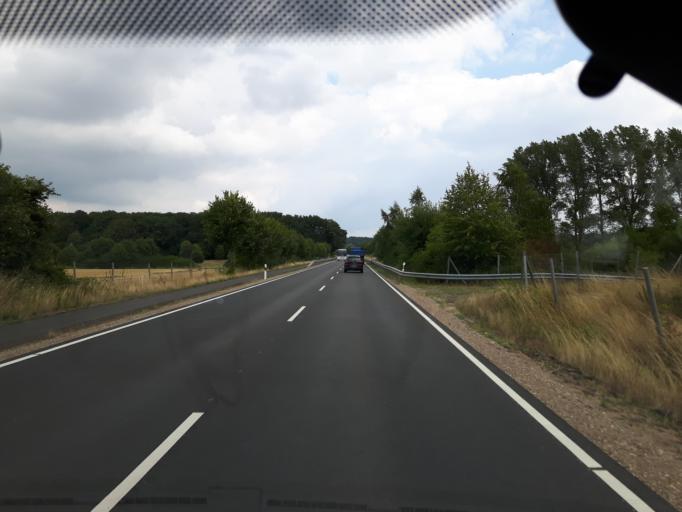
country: DE
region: Schleswig-Holstein
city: Gross Wittensee
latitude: 54.4117
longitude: 9.7835
